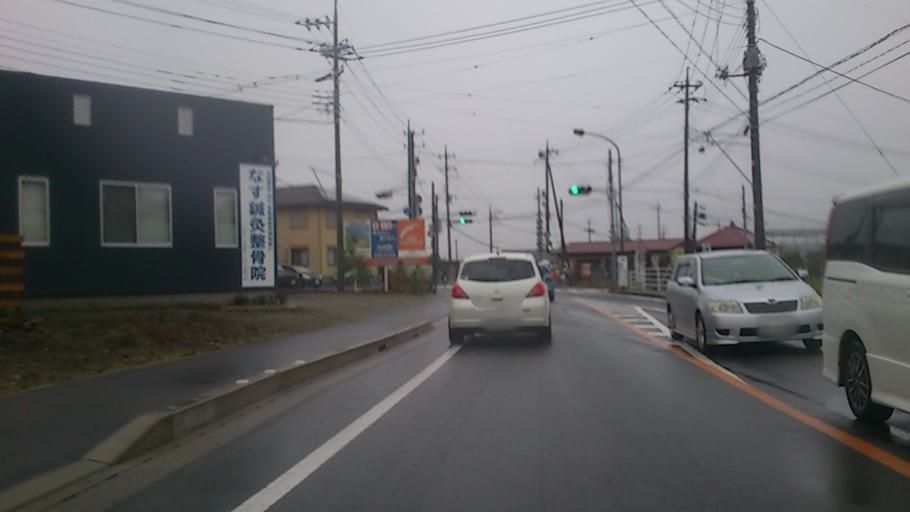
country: JP
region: Tochigi
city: Otawara
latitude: 36.8598
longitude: 140.0347
